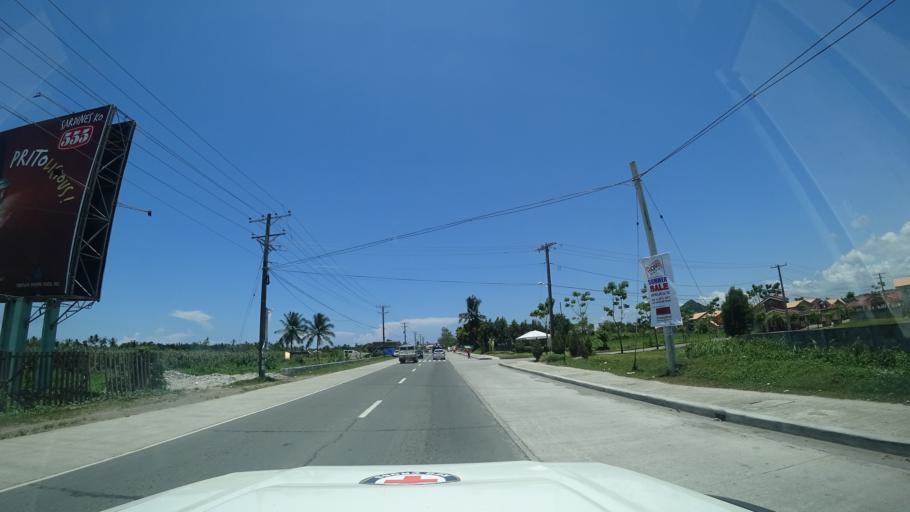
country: PH
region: Eastern Visayas
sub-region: Province of Leyte
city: Pawing
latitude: 11.1871
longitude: 124.9955
